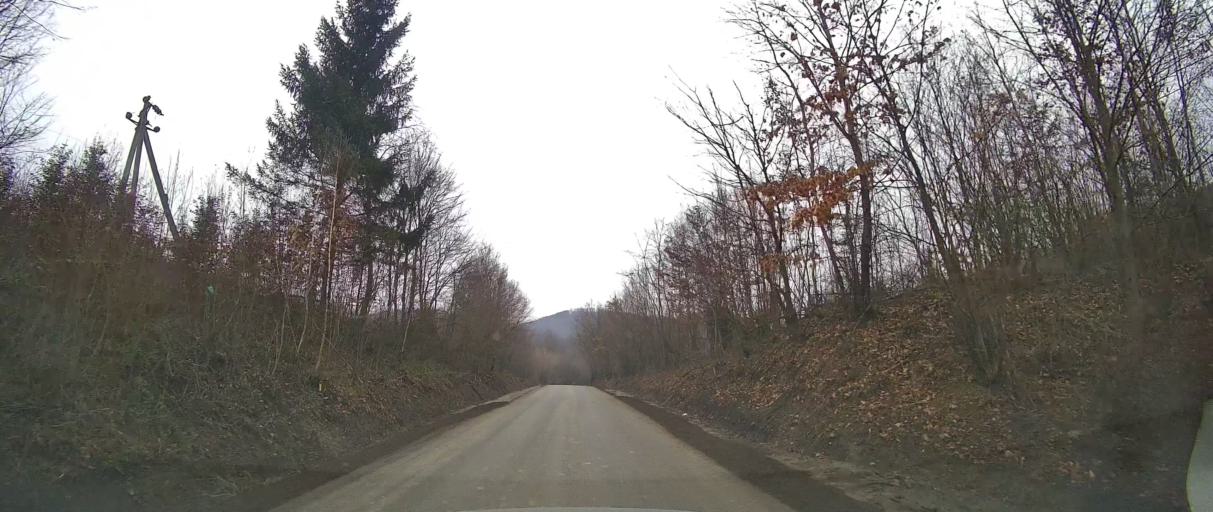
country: UA
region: Zakarpattia
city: Velykyi Bereznyi
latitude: 48.9538
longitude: 22.5470
